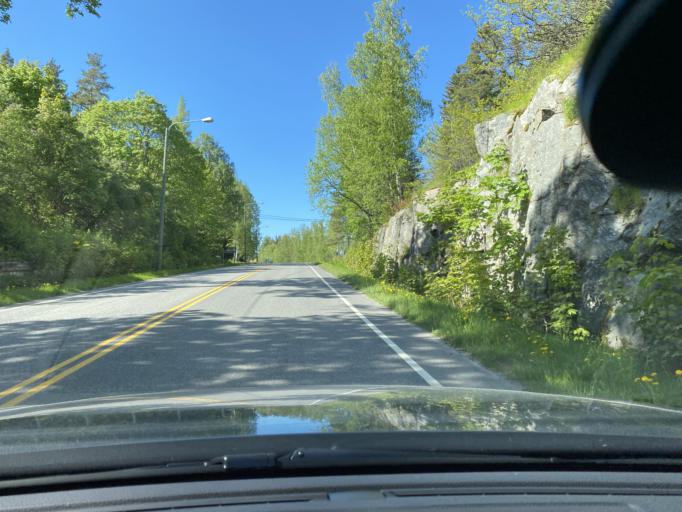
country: FI
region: Varsinais-Suomi
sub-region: Turku
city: Sauvo
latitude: 60.3463
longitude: 22.6827
